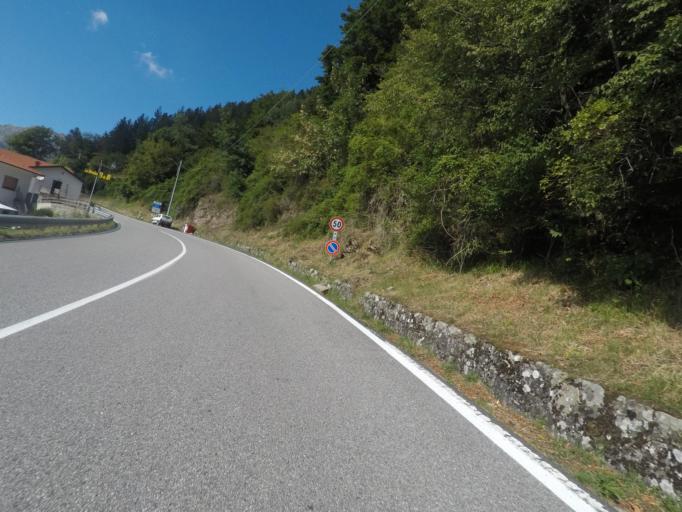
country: IT
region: Tuscany
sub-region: Provincia di Massa-Carrara
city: Comano
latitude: 44.2804
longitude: 10.1991
